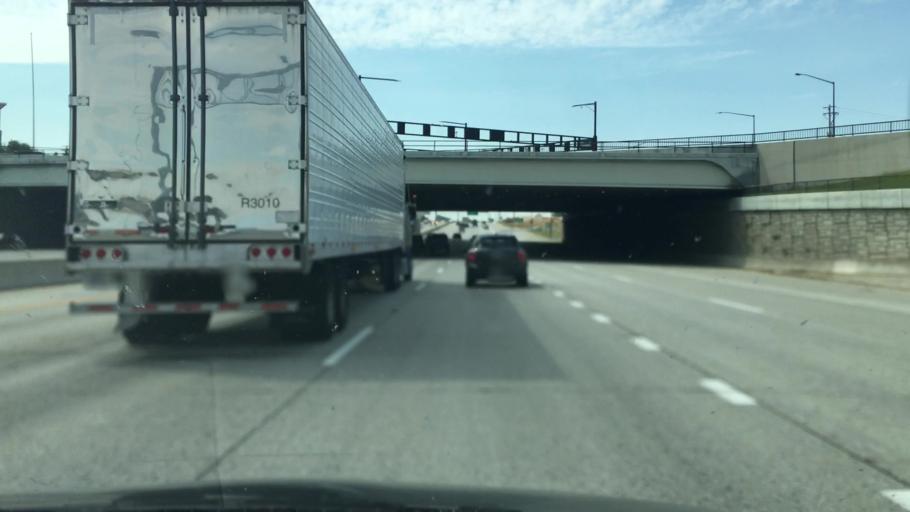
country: US
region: Idaho
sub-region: Ada County
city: Garden City
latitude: 43.5896
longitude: -116.2728
